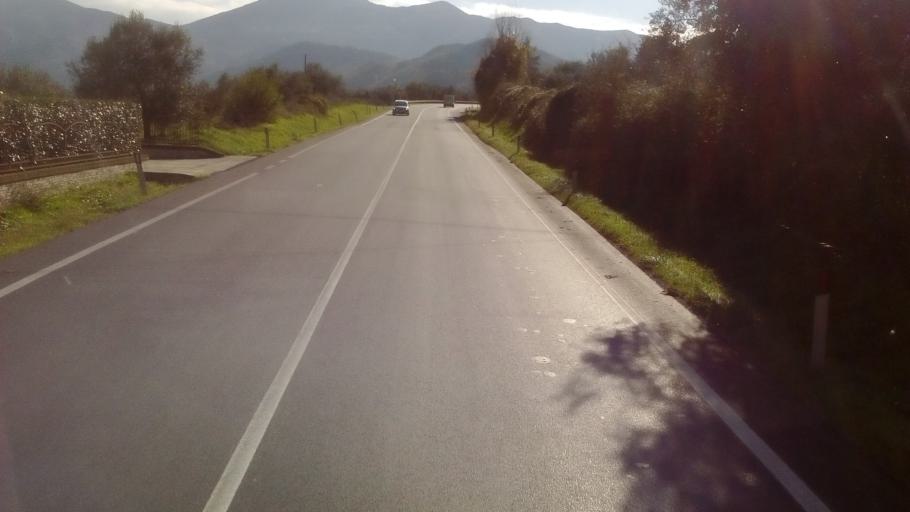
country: IT
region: Molise
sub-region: Provincia di Isernia
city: Venafro
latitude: 41.4755
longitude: 14.0300
